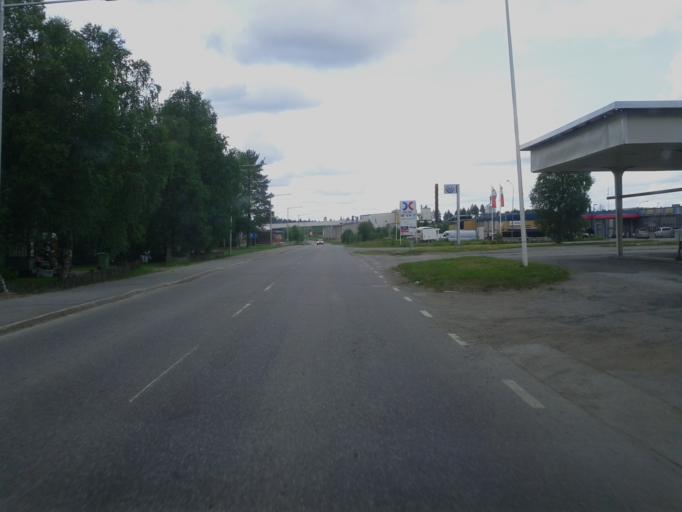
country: SE
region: Vaesterbotten
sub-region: Mala Kommun
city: Mala
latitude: 65.1909
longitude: 18.7267
